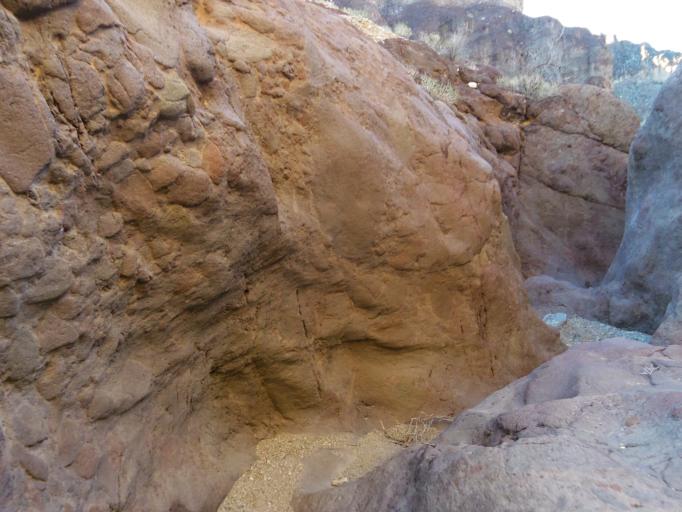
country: US
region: Nevada
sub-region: Clark County
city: Boulder City
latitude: 35.9747
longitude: -114.7115
